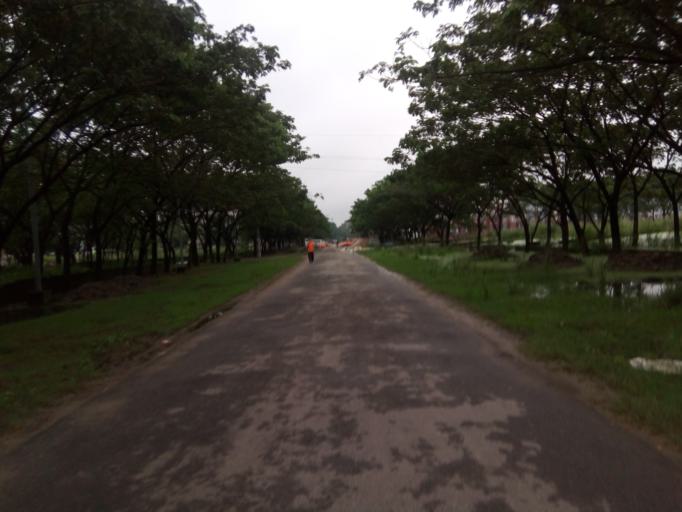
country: BD
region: Dhaka
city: Tungi
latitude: 23.8480
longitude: 90.4256
